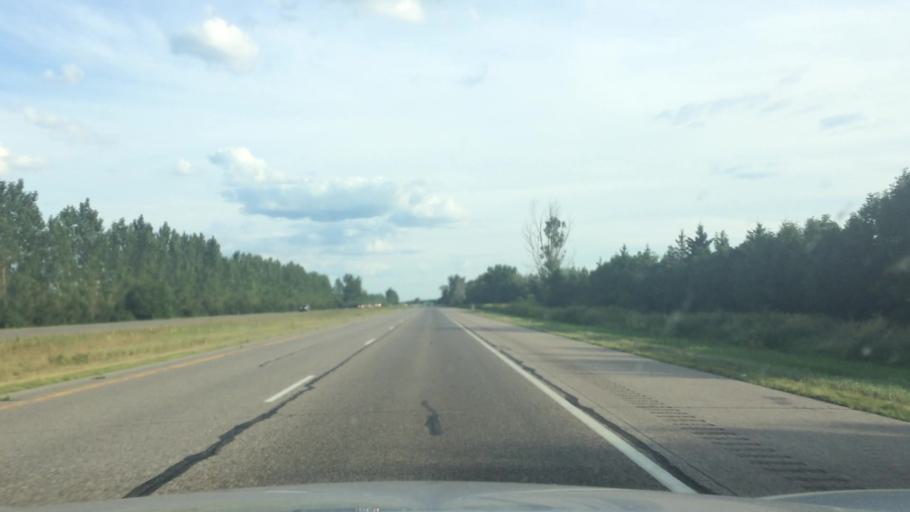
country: US
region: Wisconsin
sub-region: Portage County
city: Plover
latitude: 44.3423
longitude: -89.5225
